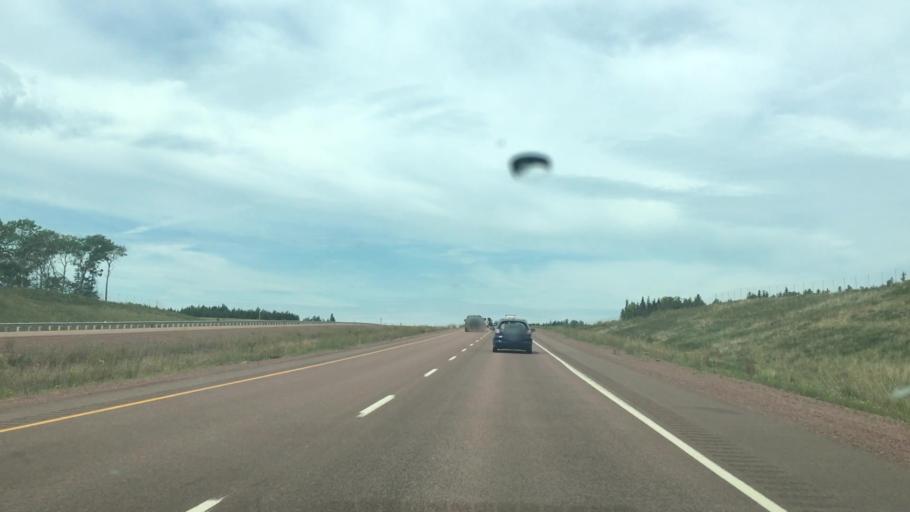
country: CA
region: Nova Scotia
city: Antigonish
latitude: 45.6048
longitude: -61.9539
